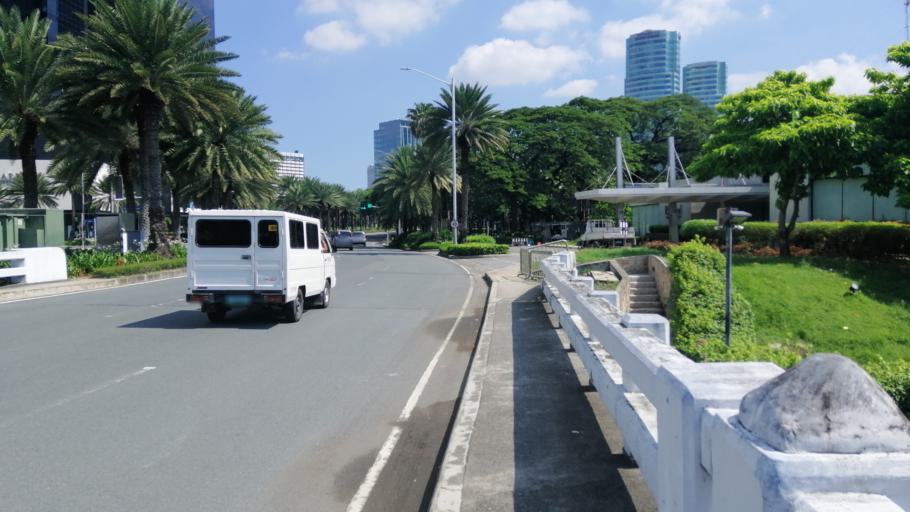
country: PH
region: Calabarzon
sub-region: Province of Laguna
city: San Pedro
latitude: 14.4145
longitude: 121.0389
